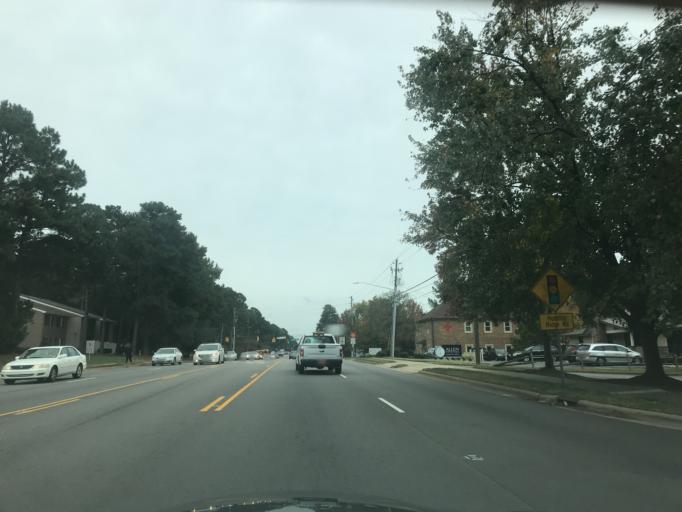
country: US
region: North Carolina
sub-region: Wake County
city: West Raleigh
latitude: 35.8767
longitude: -78.6239
